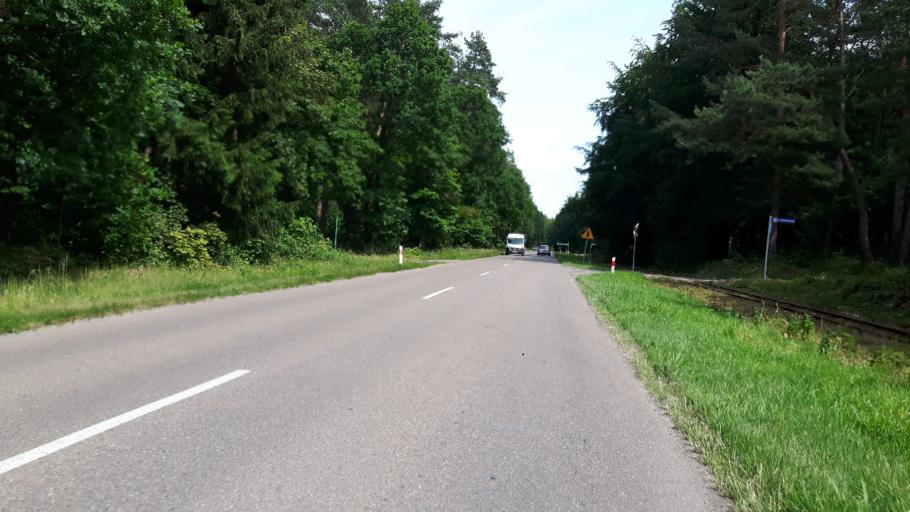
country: PL
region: Pomeranian Voivodeship
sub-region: Powiat nowodworski
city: Stegna
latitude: 54.3319
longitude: 19.0795
